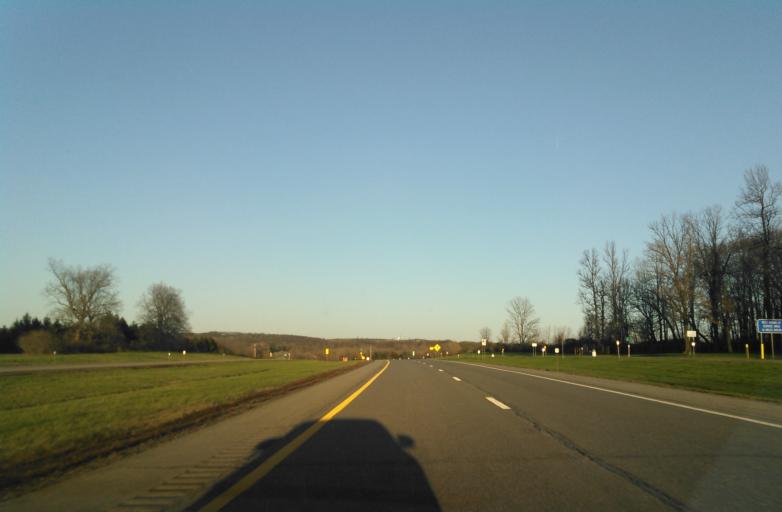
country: US
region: New York
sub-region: Ontario County
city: Victor
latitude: 43.0151
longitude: -77.4803
